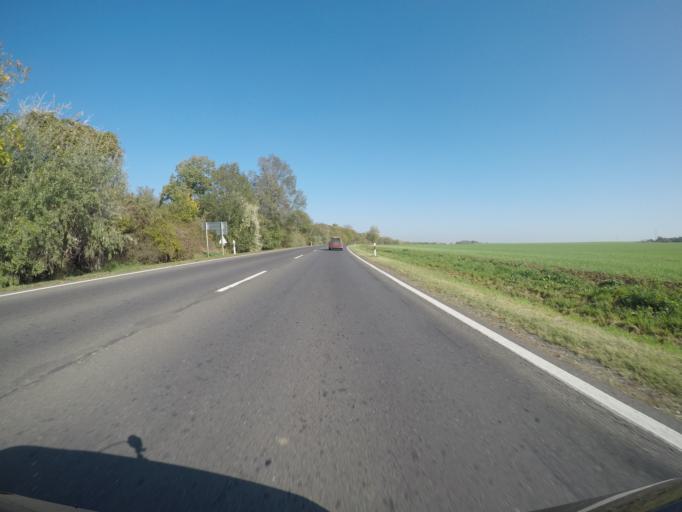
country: HU
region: Baranya
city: Hosszuheteny
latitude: 46.1286
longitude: 18.3710
